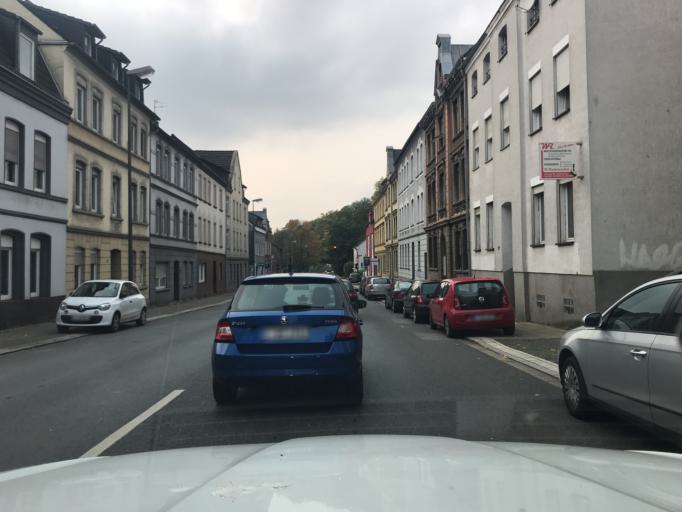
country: DE
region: North Rhine-Westphalia
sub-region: Regierungsbezirk Dusseldorf
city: Velbert
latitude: 51.3886
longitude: 7.0170
